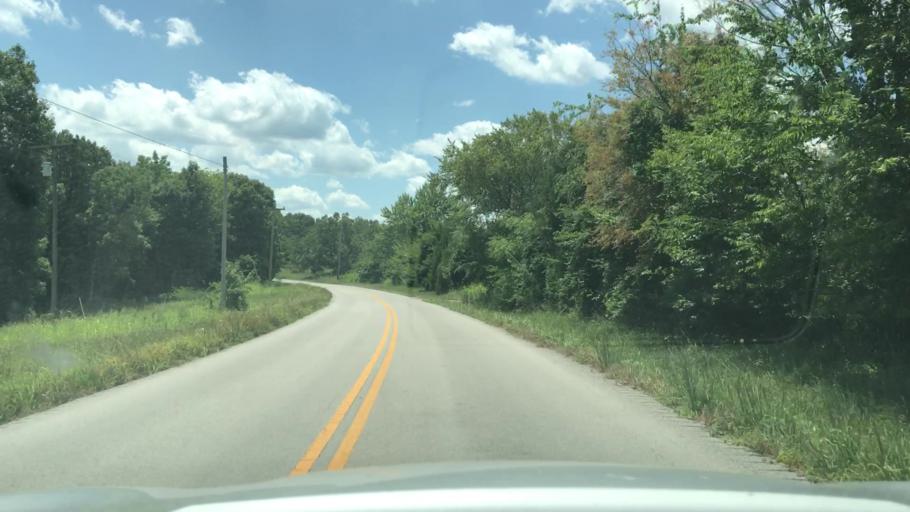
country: US
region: Kentucky
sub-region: Hopkins County
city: Nortonville
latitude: 37.1132
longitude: -87.3312
